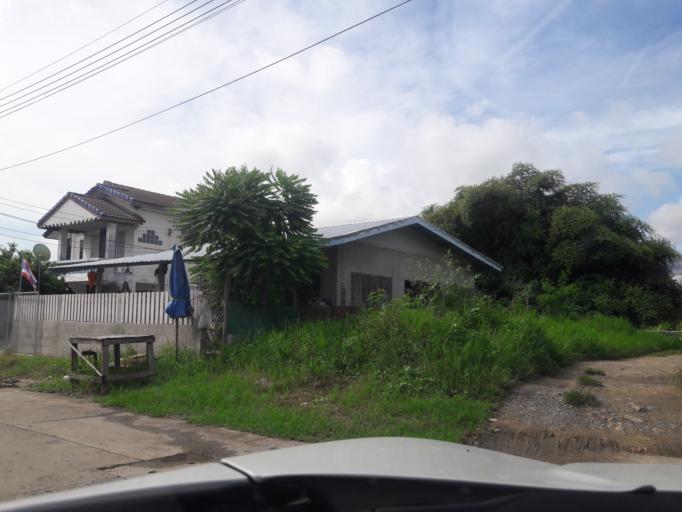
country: TH
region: Nakhon Sawan
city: Tak Fa
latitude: 15.3424
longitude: 100.4961
